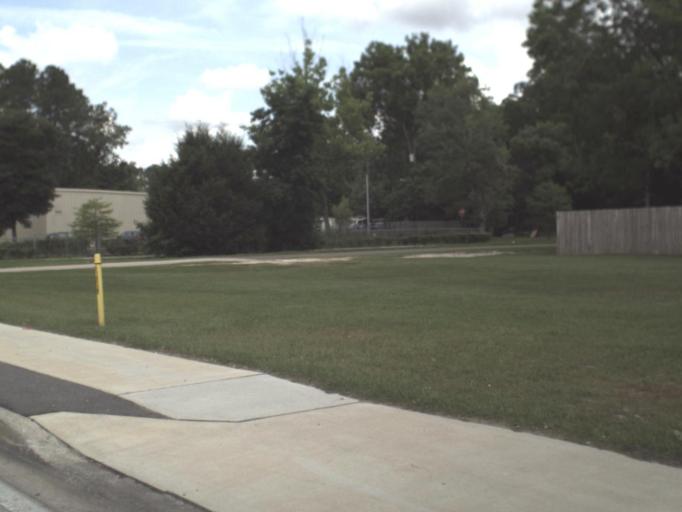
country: US
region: Florida
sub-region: Duval County
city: Jacksonville
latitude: 30.4387
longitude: -81.6999
